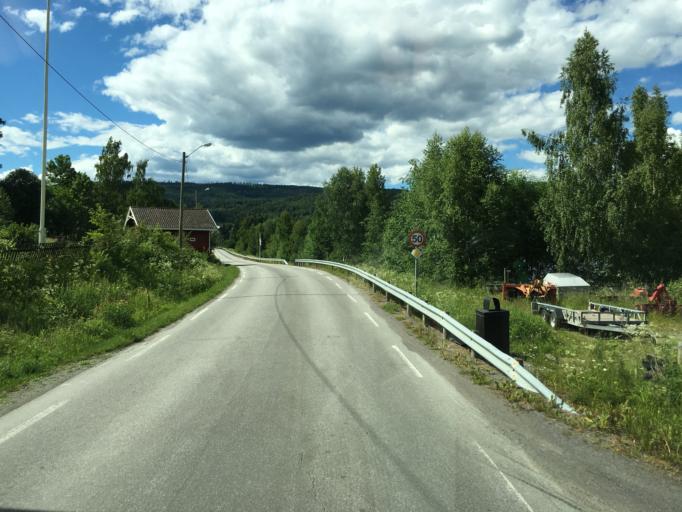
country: NO
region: Oppland
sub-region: Sondre Land
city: Hov
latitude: 60.5176
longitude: 10.2968
